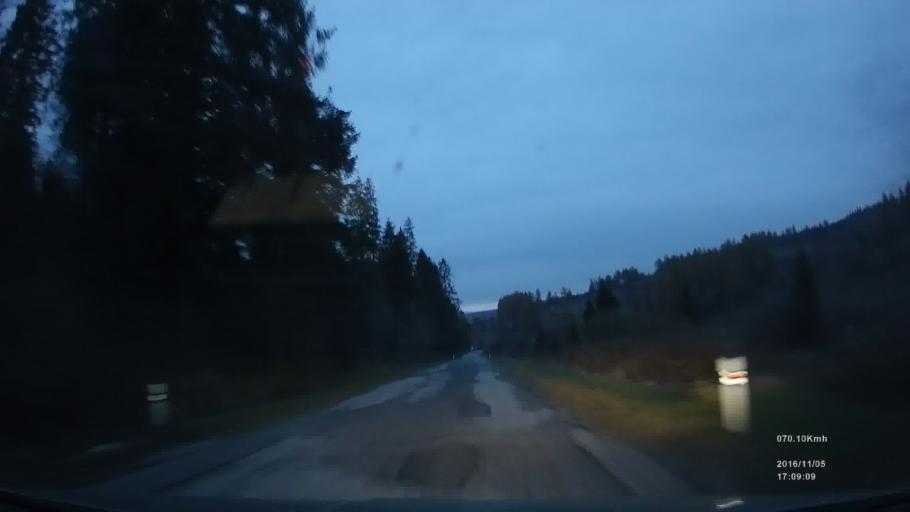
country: SK
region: Presovsky
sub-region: Okres Presov
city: Levoca
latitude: 49.0519
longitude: 20.5167
